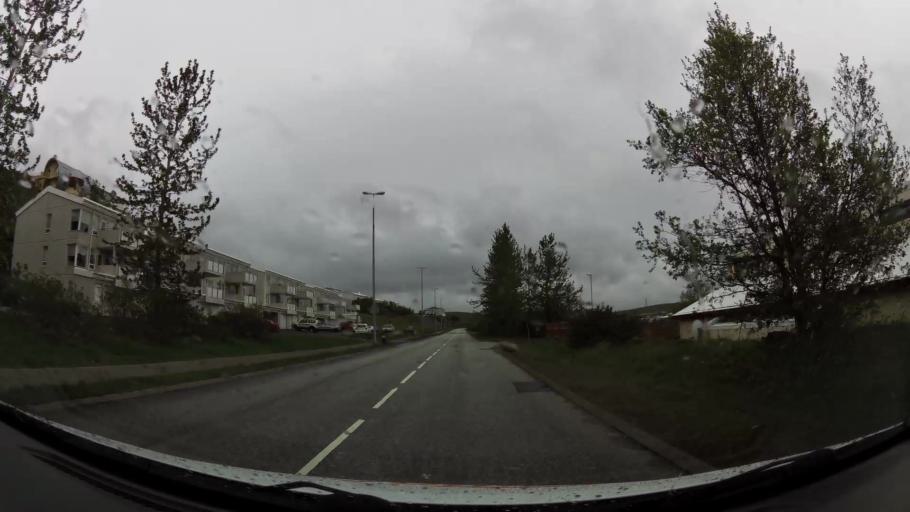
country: IS
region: Capital Region
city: Hafnarfjoerdur
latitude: 64.0642
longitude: -21.9274
